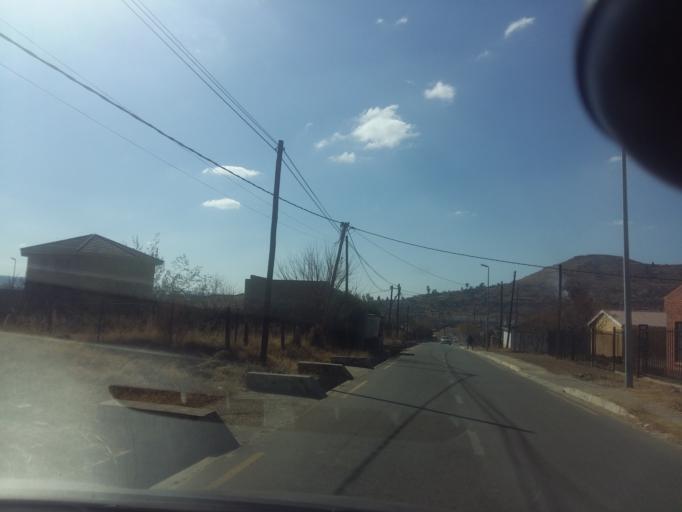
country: LS
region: Maseru
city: Maseru
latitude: -29.3399
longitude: 27.4520
